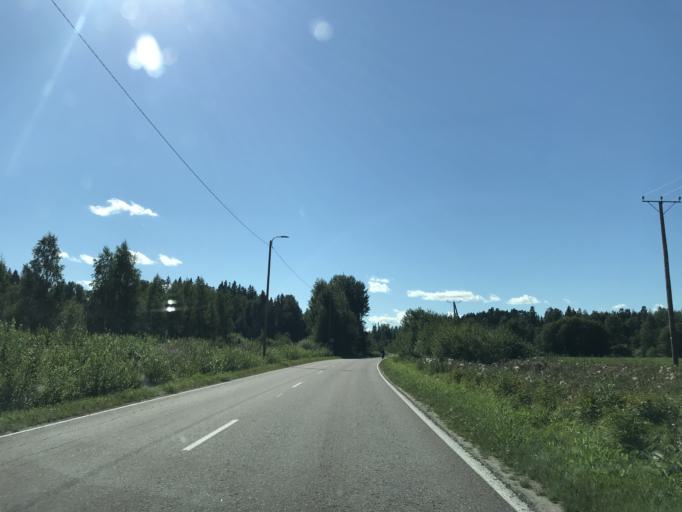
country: FI
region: Uusimaa
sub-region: Helsinki
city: Nurmijaervi
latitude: 60.4890
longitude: 24.6109
